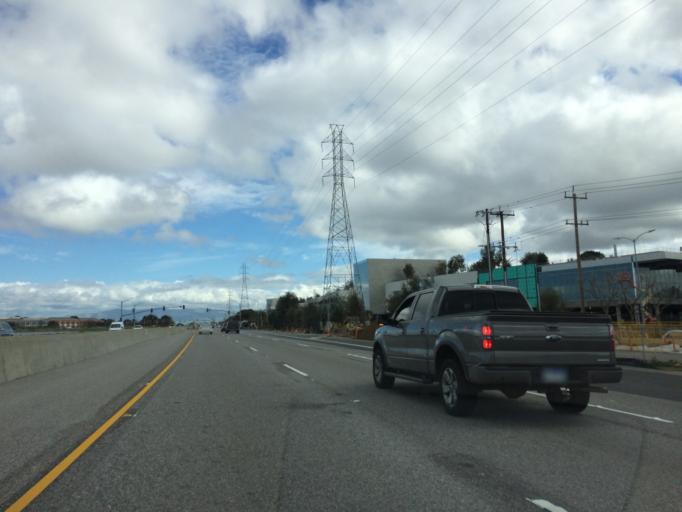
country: US
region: California
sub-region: San Mateo County
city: East Palo Alto
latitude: 37.4819
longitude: -122.1580
